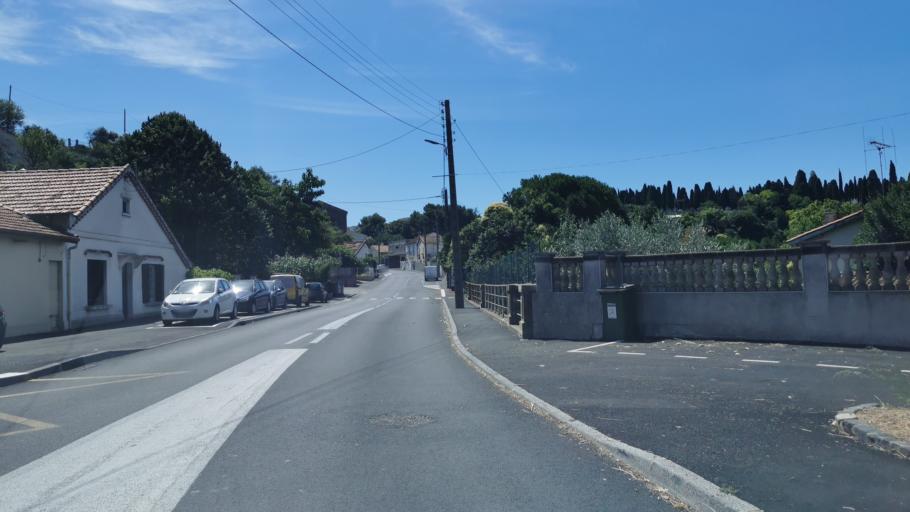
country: FR
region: Languedoc-Roussillon
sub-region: Departement de l'Herault
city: Beziers
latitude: 43.3538
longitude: 3.2127
